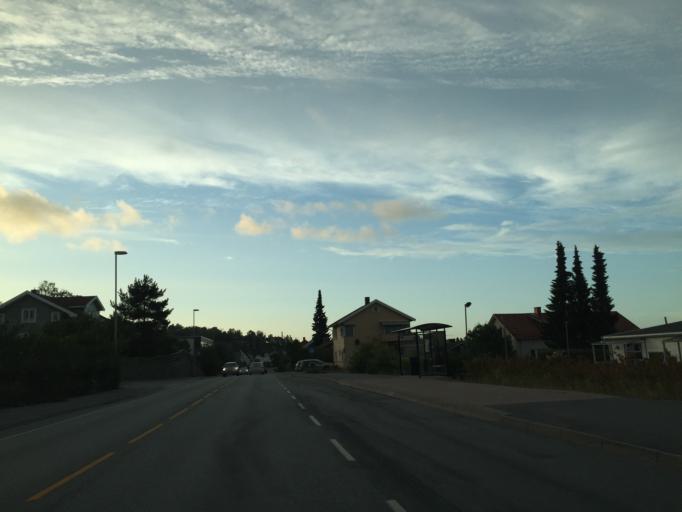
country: NO
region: Ostfold
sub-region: Fredrikstad
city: Fredrikstad
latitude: 59.1999
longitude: 10.9406
